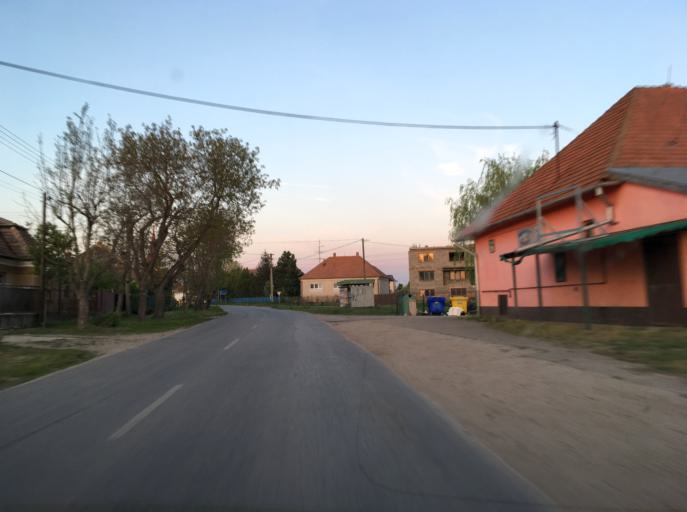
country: SK
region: Nitriansky
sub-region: Okres Nove Zamky
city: Nove Zamky
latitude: 47.9241
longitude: 18.1152
